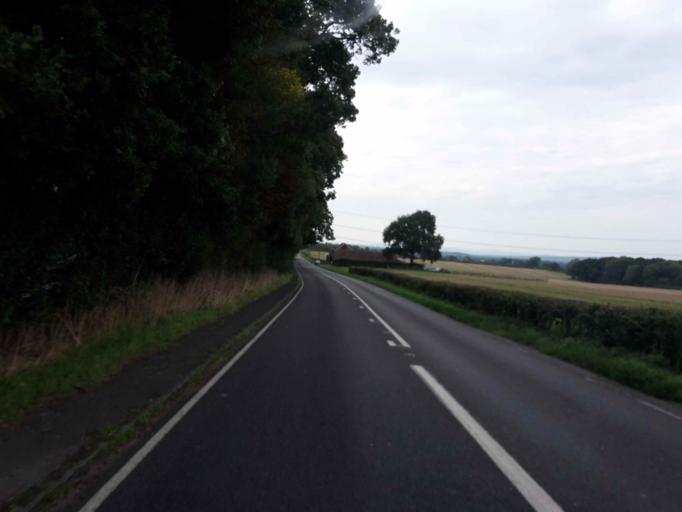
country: GB
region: England
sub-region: West Sussex
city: Billingshurst
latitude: 51.0336
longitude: -0.4435
